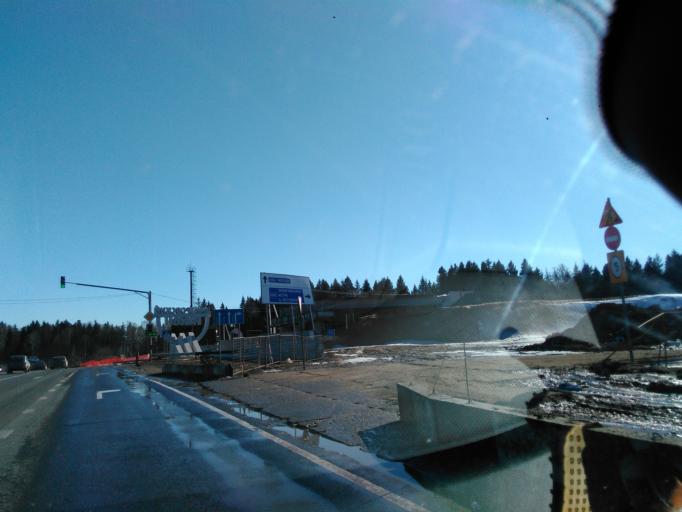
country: RU
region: Moskovskaya
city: Yermolino
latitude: 56.1394
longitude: 37.4948
